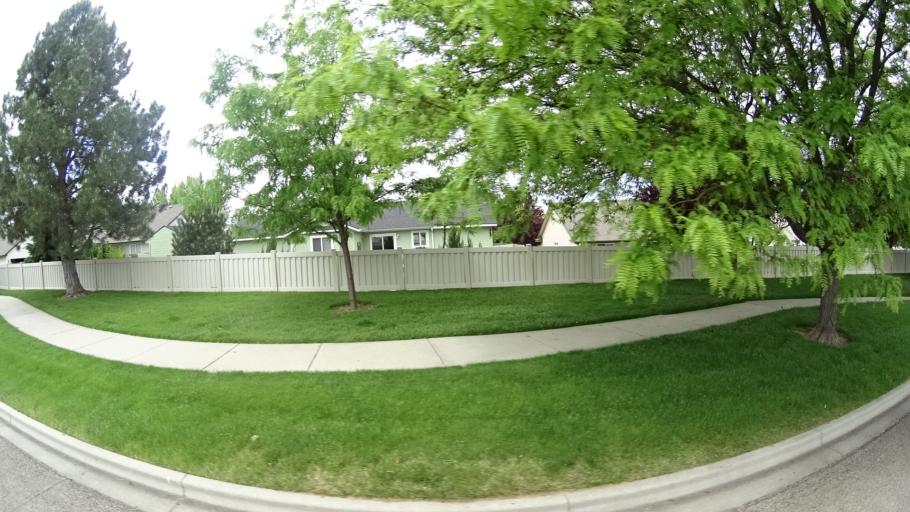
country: US
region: Idaho
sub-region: Ada County
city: Kuna
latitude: 43.4852
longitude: -116.4337
